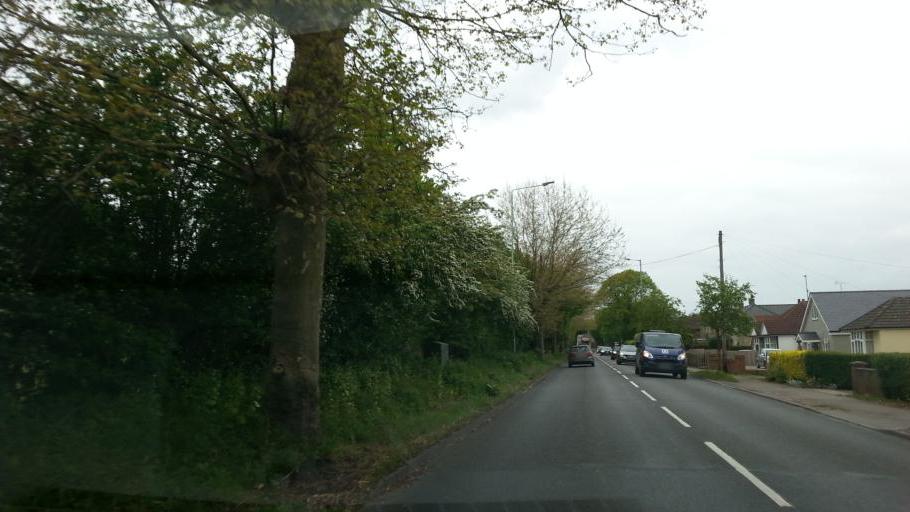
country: GB
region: England
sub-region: Suffolk
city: Bury St Edmunds
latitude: 52.2313
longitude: 0.7297
